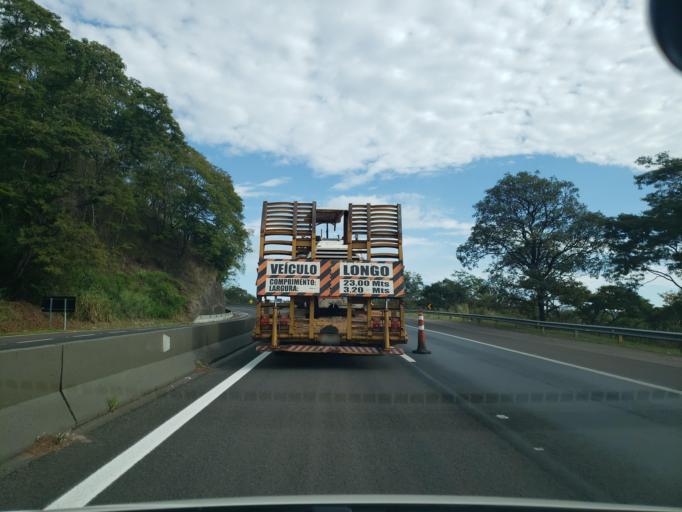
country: BR
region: Sao Paulo
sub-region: Dois Corregos
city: Dois Corregos
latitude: -22.2482
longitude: -48.3475
